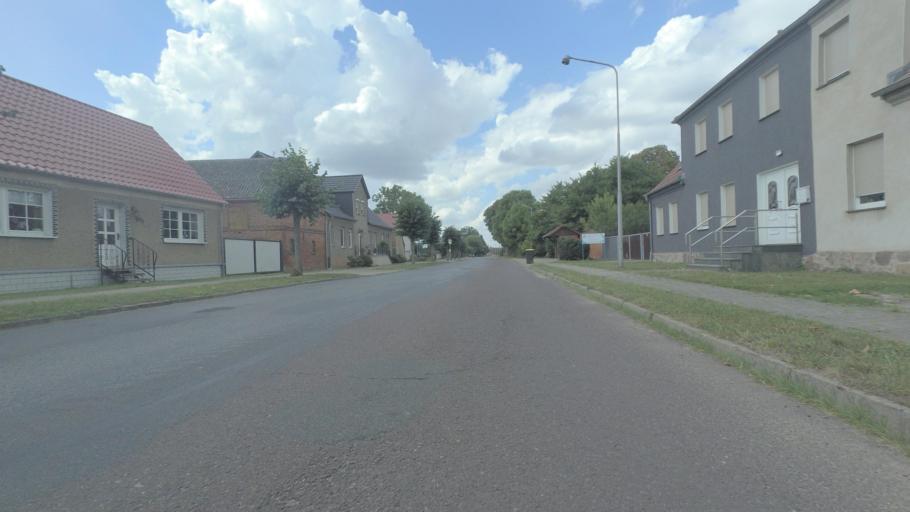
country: DE
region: Brandenburg
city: Wittstock
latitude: 53.2415
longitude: 12.4279
